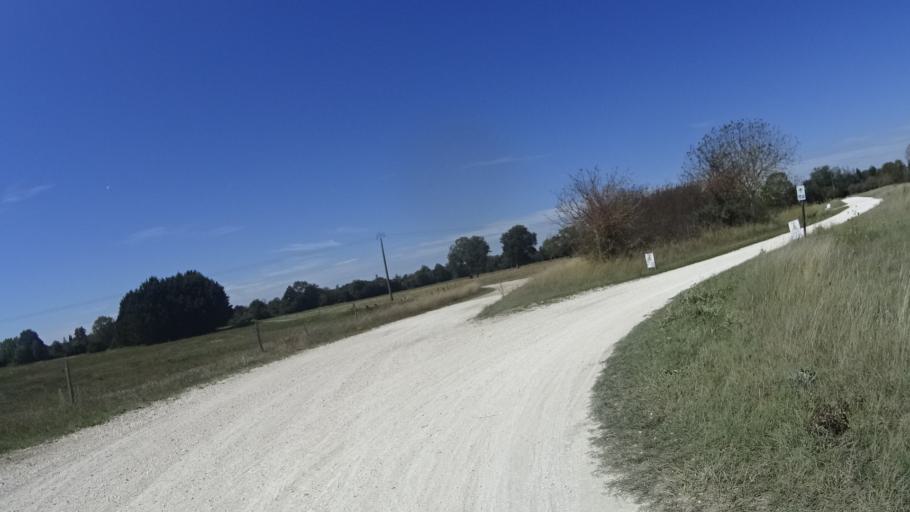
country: FR
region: Centre
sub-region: Departement du Loiret
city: Bonny-sur-Loire
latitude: 47.5342
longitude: 2.8468
